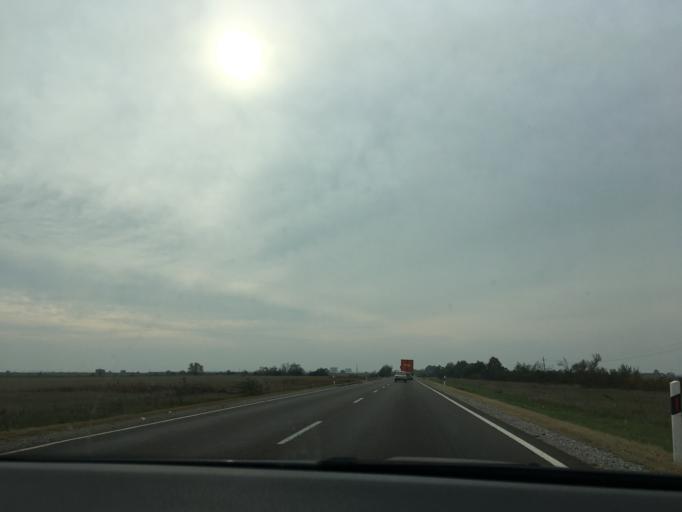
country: HU
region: Jasz-Nagykun-Szolnok
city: Kisujszallas
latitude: 47.2475
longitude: 20.8347
